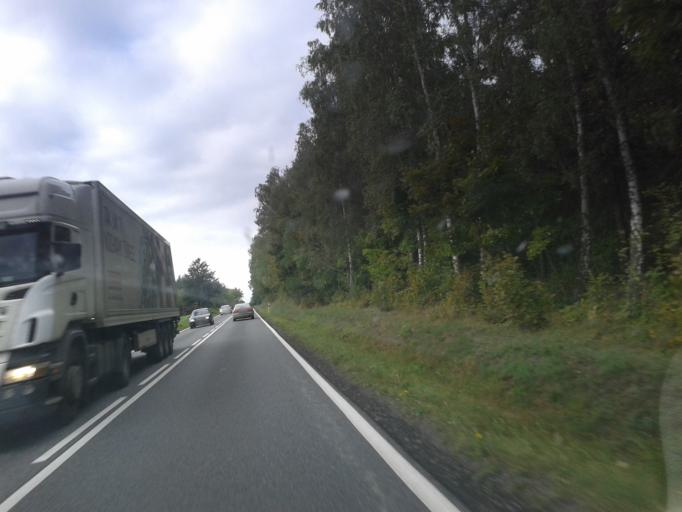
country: PL
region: Kujawsko-Pomorskie
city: Kamien Krajenski
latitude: 53.5438
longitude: 17.5138
